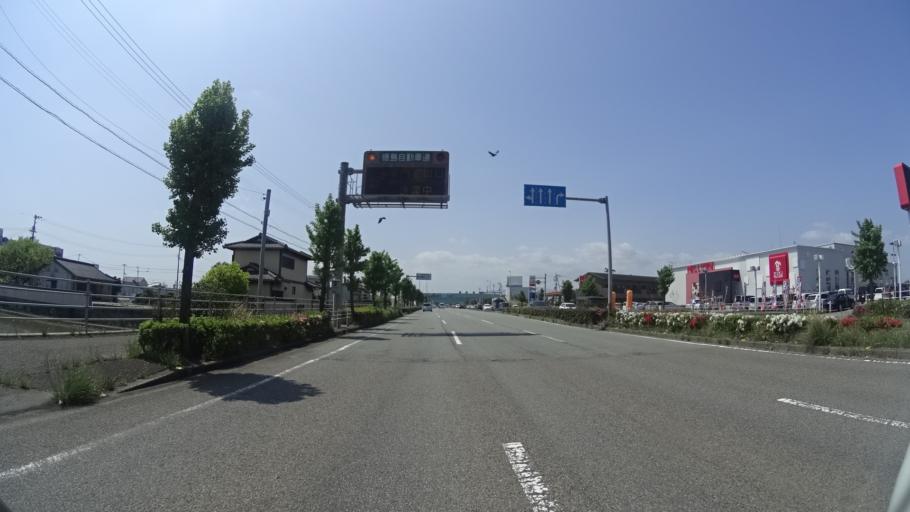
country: JP
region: Tokushima
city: Tokushima-shi
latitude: 34.1072
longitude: 134.5765
